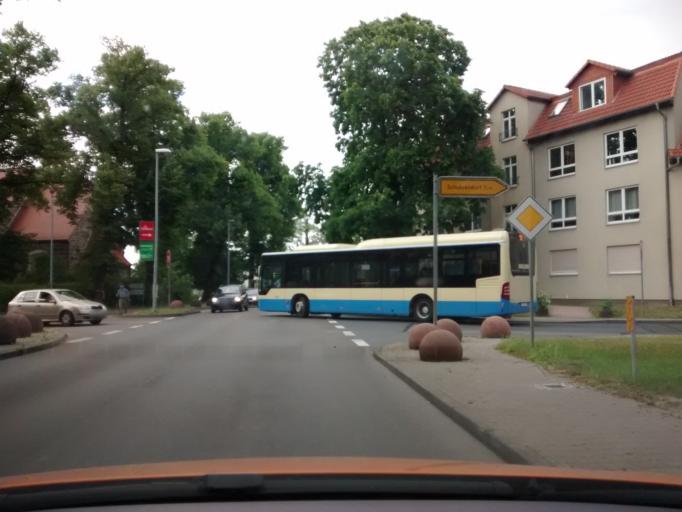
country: DE
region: Brandenburg
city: Schulzendorf
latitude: 52.3614
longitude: 13.5564
